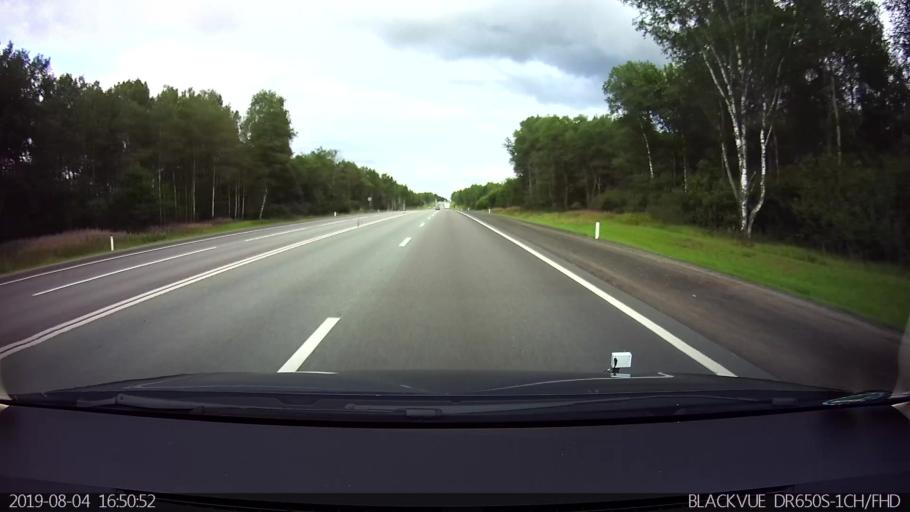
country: RU
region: Smolensk
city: Vyaz'ma
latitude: 55.2168
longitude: 34.1975
